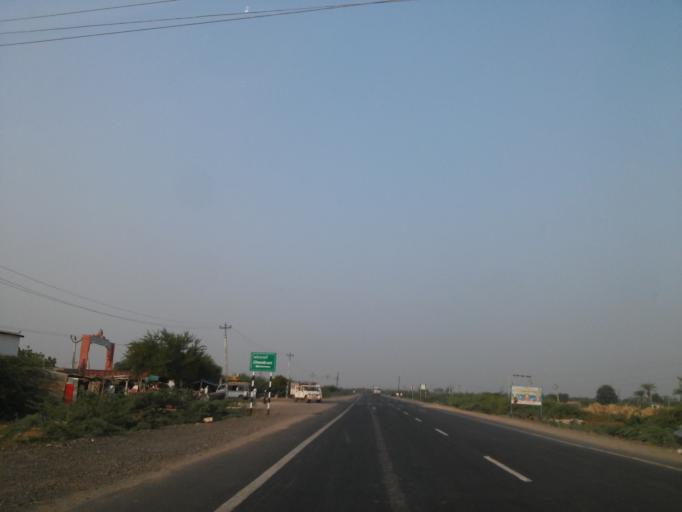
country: IN
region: Gujarat
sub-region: Kachchh
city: Anjar
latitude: 23.2958
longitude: 70.0632
